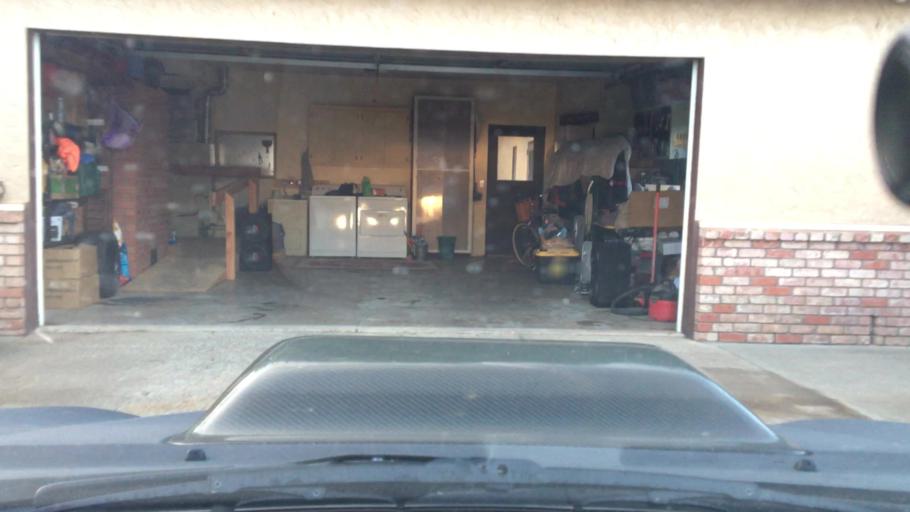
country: US
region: California
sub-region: Butte County
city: Chico
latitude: 39.7080
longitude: -121.8362
